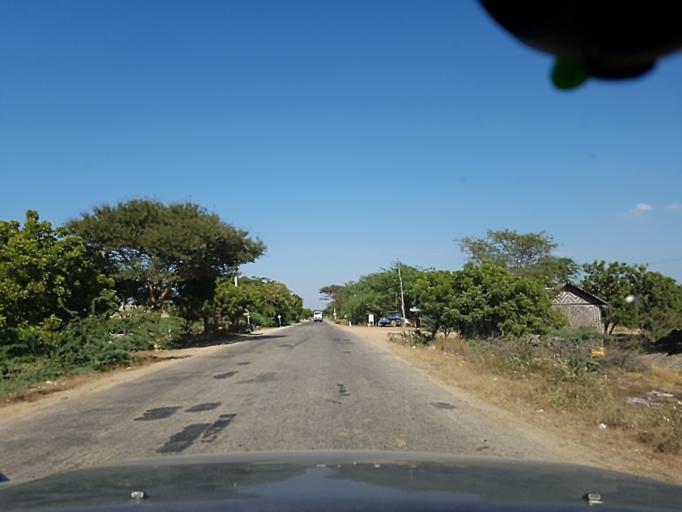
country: MM
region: Sagain
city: Monywa
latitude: 21.8735
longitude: 95.2686
